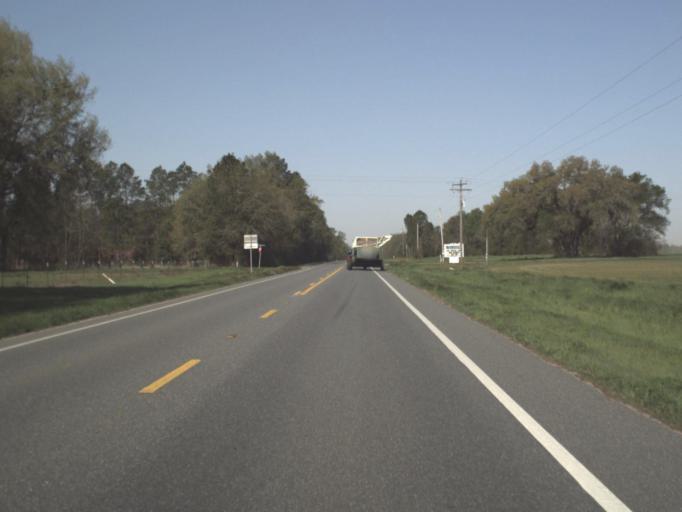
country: US
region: Florida
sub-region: Jackson County
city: Malone
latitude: 30.9596
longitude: -85.1953
